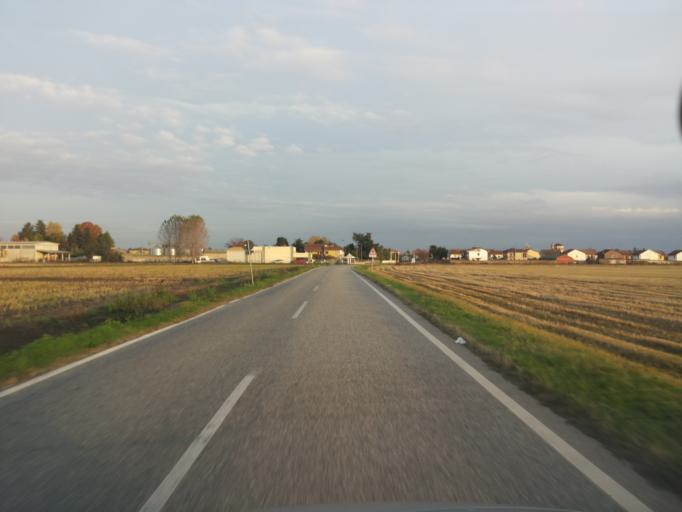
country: IT
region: Piedmont
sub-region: Provincia di Vercelli
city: Costanzana
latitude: 45.2403
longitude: 8.3610
